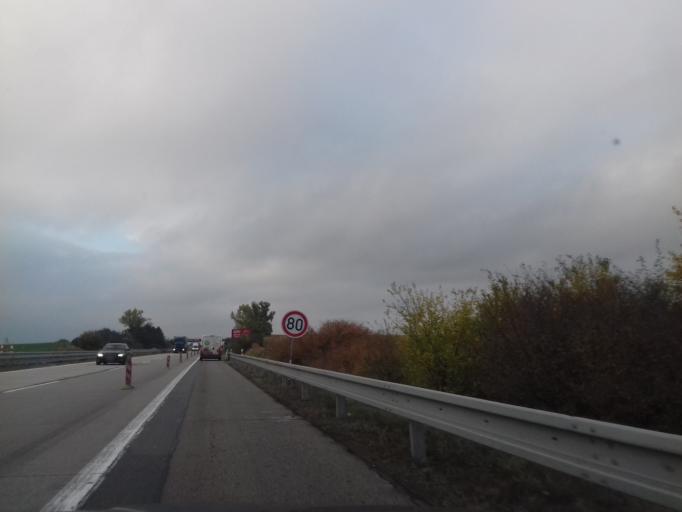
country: CZ
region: South Moravian
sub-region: Okres Brno-Venkov
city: Blucina
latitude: 49.0709
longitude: 16.6628
